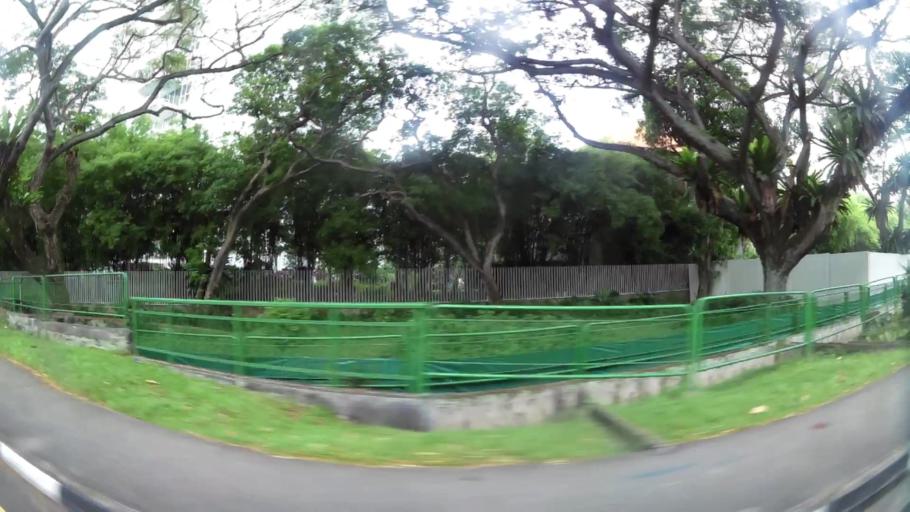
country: SG
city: Singapore
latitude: 1.3008
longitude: 103.9024
